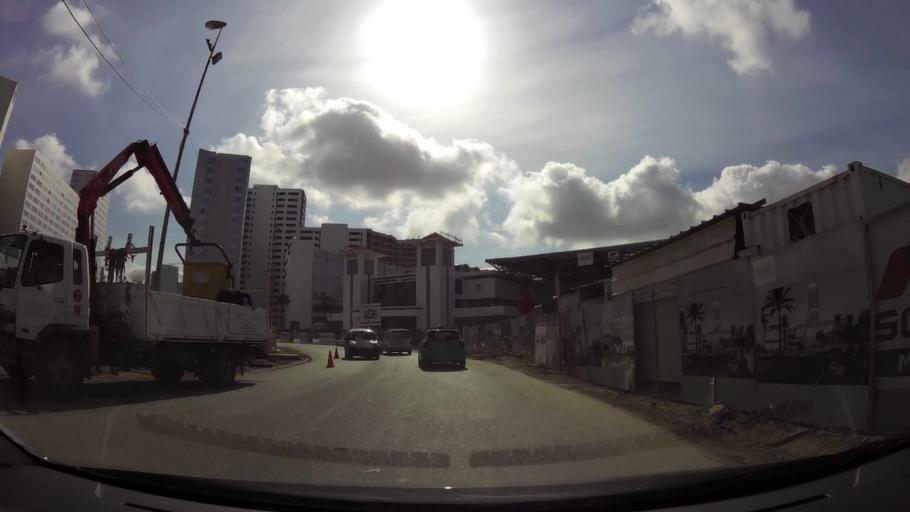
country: MA
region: Tanger-Tetouan
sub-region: Tanger-Assilah
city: Tangier
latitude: 35.7718
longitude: -5.7873
